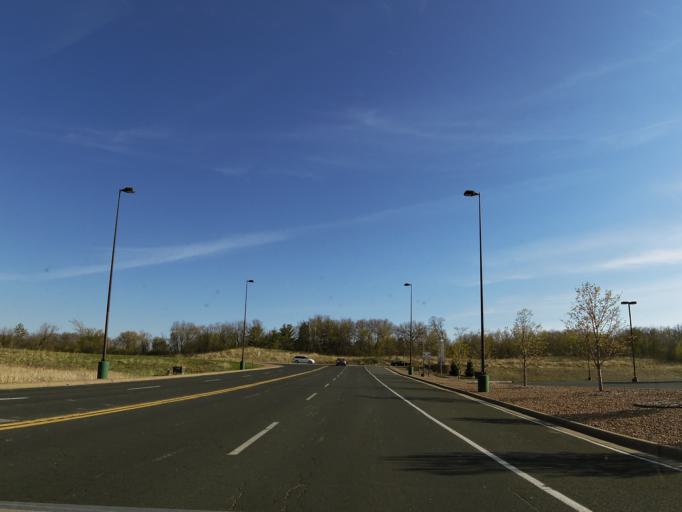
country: US
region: Minnesota
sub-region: Scott County
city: Prior Lake
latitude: 44.7248
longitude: -93.4749
